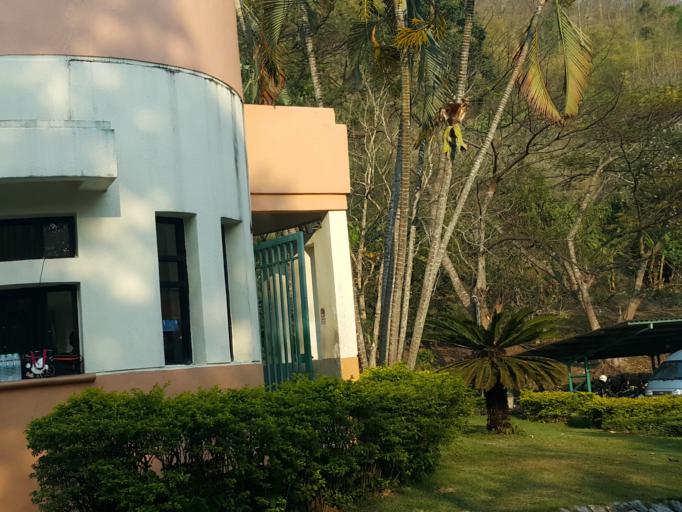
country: TH
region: Chiang Mai
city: Samoeng
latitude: 18.9045
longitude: 98.8292
